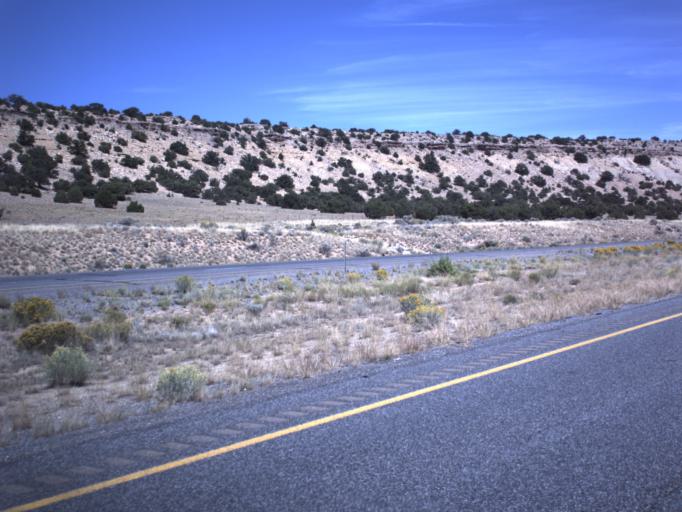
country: US
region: Utah
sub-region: Emery County
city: Castle Dale
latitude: 38.9051
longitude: -110.5477
